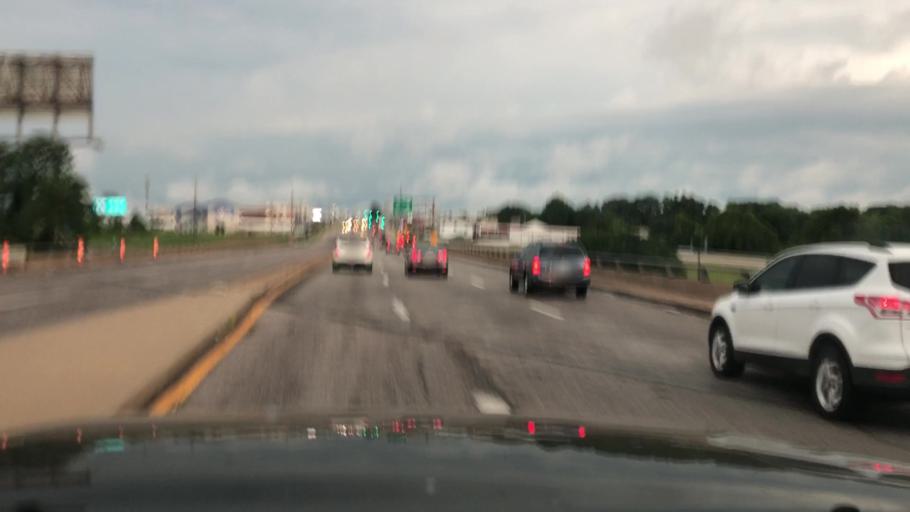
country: US
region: Missouri
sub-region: Saint Louis County
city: Bridgeton
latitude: 38.7443
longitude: -90.4135
